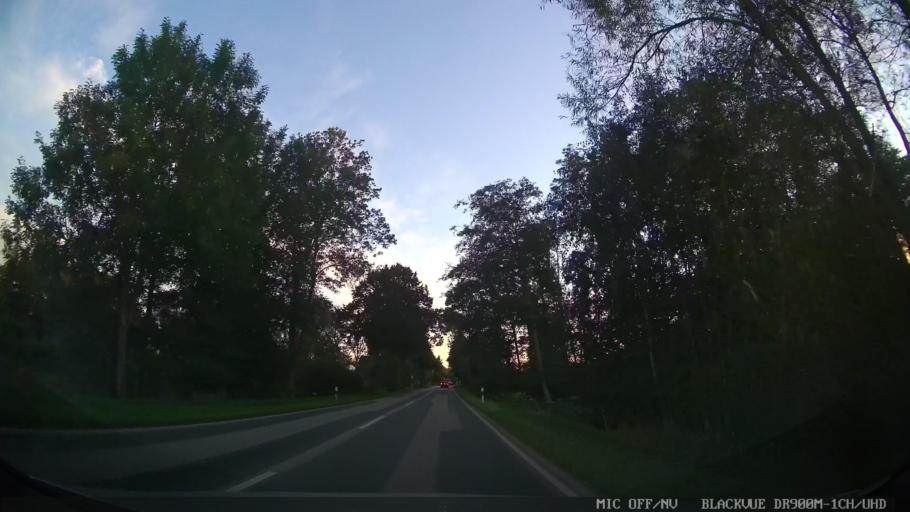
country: DE
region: Schleswig-Holstein
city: Susel
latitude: 54.0622
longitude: 10.6861
